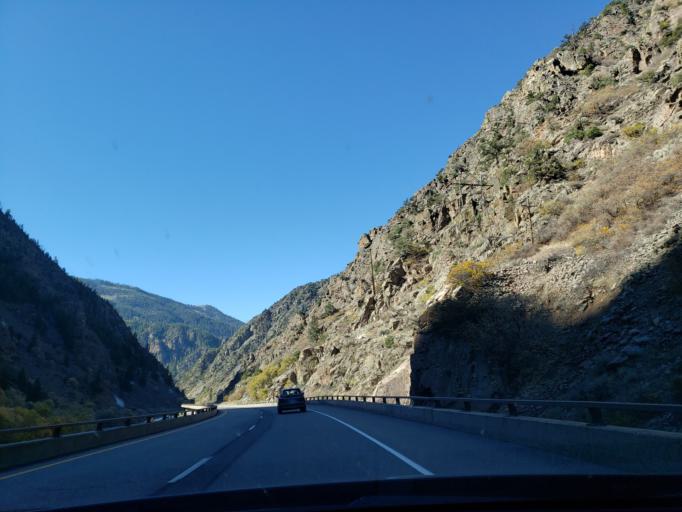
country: US
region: Colorado
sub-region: Garfield County
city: Glenwood Springs
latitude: 39.5695
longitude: -107.2276
